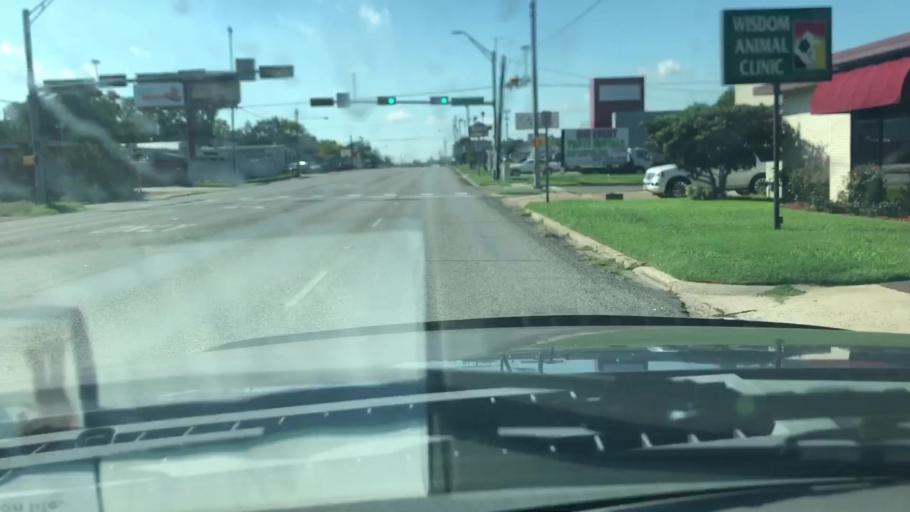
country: US
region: Arkansas
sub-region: Miller County
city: Texarkana
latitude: 33.4404
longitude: -94.0532
